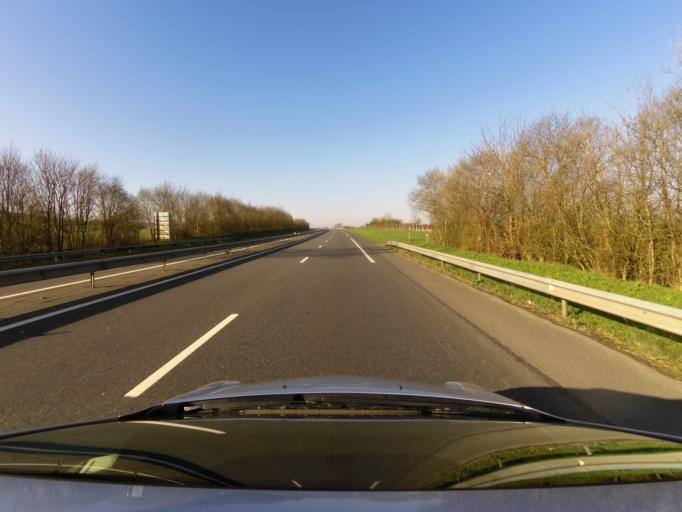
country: FR
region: Lower Normandy
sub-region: Departement du Calvados
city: Saint-Martin-des-Besaces
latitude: 49.0314
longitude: -0.8242
